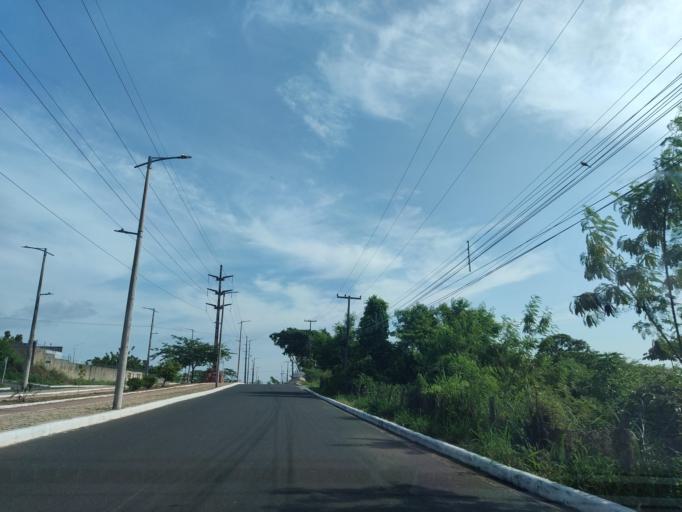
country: BR
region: Piaui
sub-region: Teresina
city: Teresina
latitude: -5.0767
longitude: -42.7516
